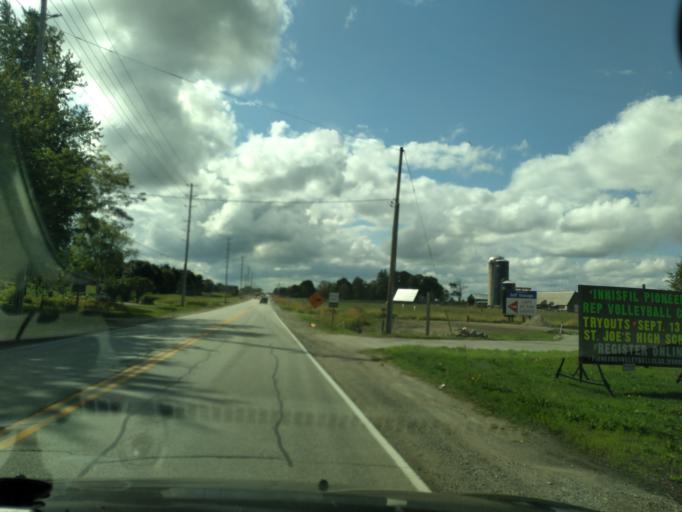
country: CA
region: Ontario
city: Innisfil
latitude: 44.3028
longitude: -79.6013
